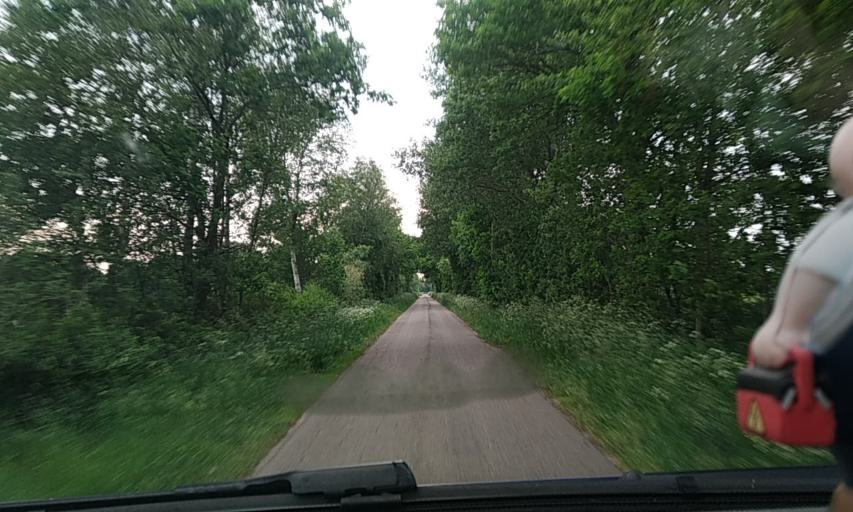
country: DE
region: Schleswig-Holstein
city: Borm
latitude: 54.3865
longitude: 9.3923
